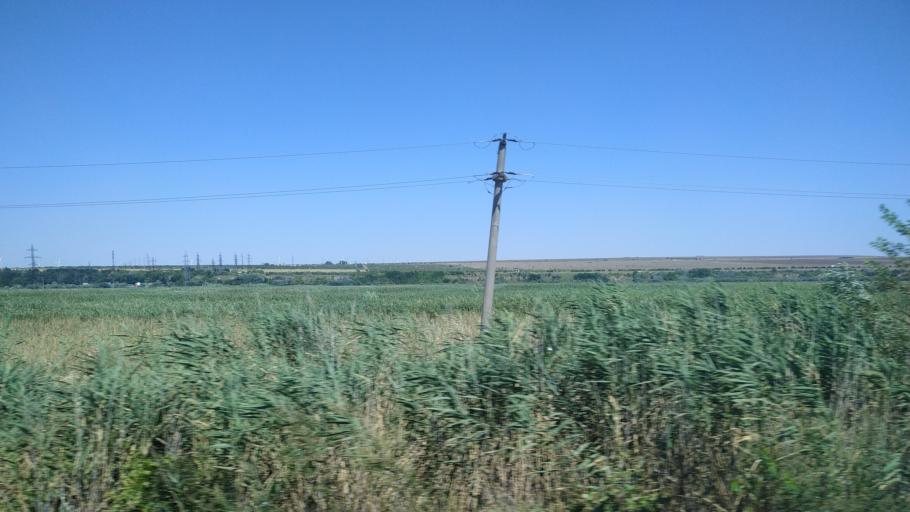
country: RO
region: Constanta
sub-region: Comuna Mircea Voda
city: Satu Nou
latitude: 44.2616
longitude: 28.2004
